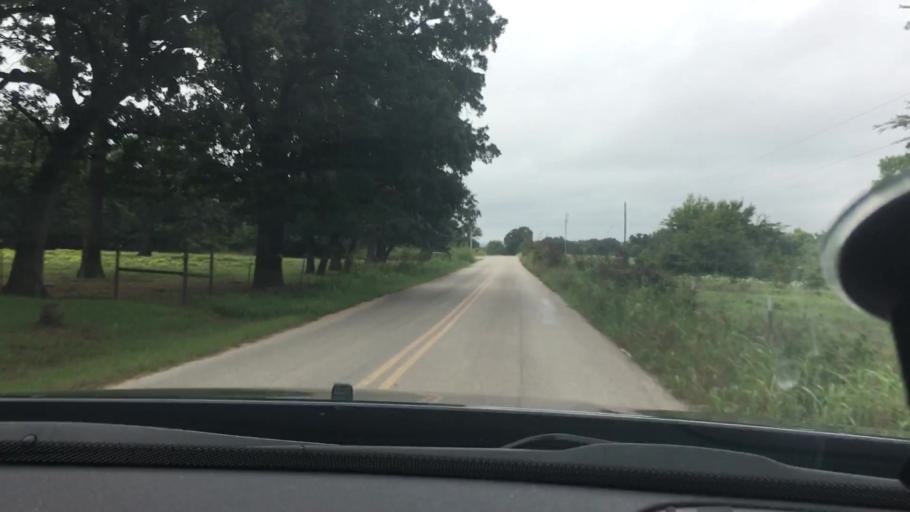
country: US
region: Oklahoma
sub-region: Pontotoc County
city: Ada
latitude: 34.8075
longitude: -96.7573
